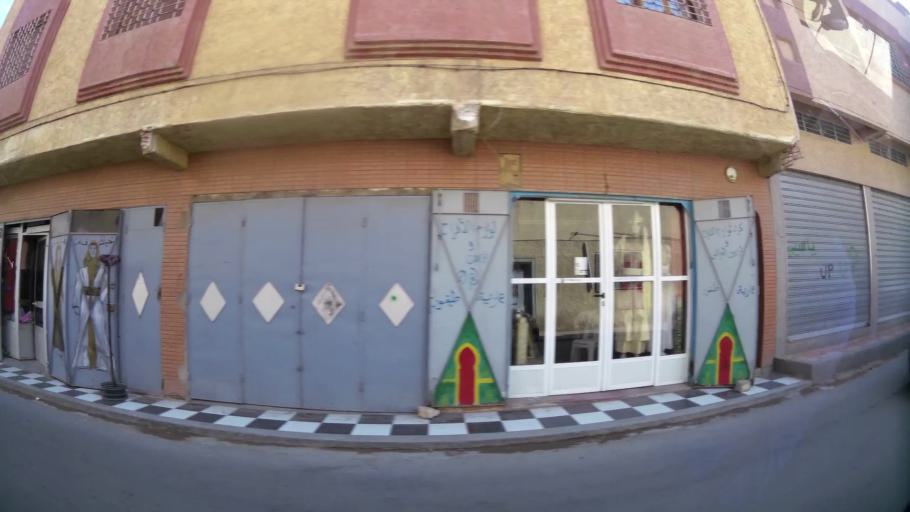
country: MA
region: Oriental
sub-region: Oujda-Angad
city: Oujda
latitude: 34.7118
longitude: -1.8856
